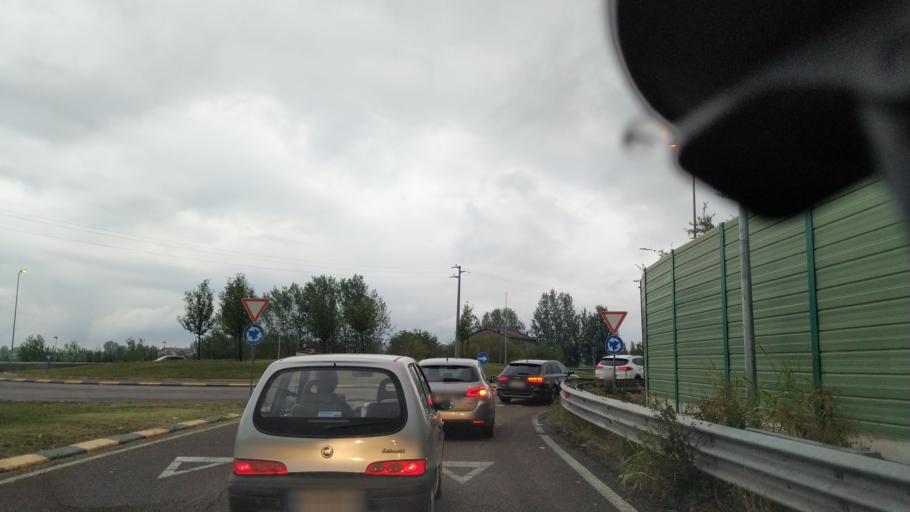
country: IT
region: Emilia-Romagna
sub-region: Provincia di Modena
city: Nonantola
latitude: 44.6736
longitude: 11.0100
